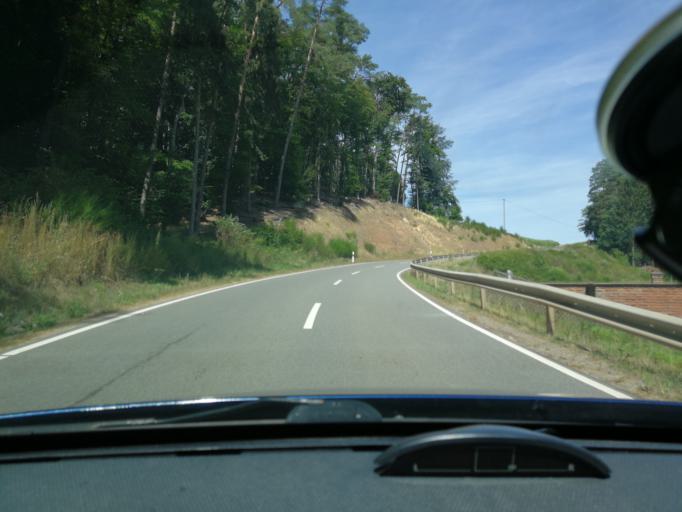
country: DE
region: Rheinland-Pfalz
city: Heidweiler
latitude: 49.9248
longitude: 6.7534
